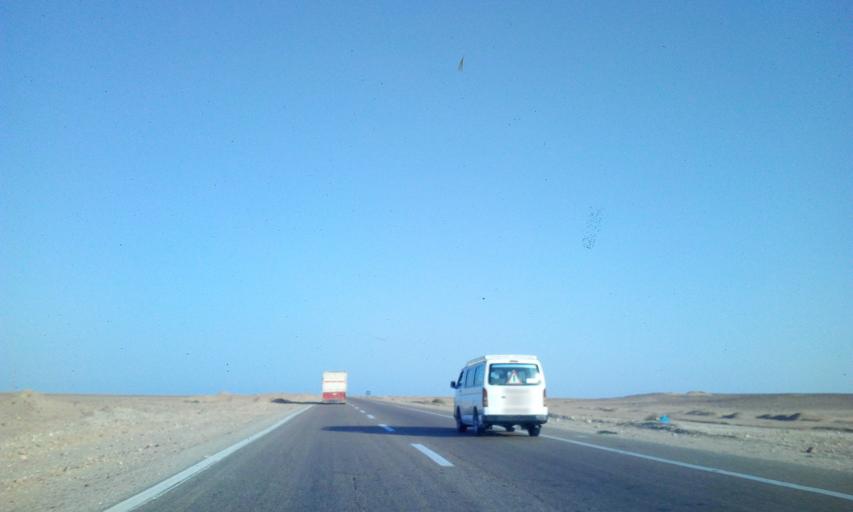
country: EG
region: South Sinai
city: Tor
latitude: 28.5484
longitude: 32.8997
